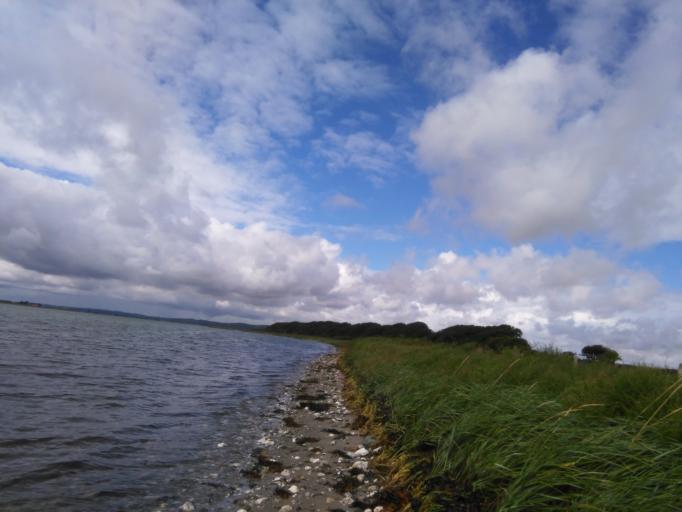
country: DK
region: Central Jutland
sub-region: Odder Kommune
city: Odder
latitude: 55.8539
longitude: 10.1499
